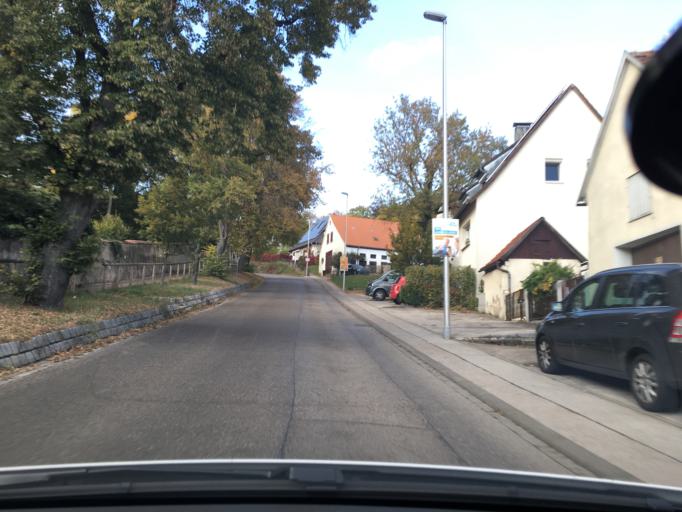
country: DE
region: Bavaria
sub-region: Regierungsbezirk Mittelfranken
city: Ansbach
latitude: 49.3062
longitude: 10.5777
